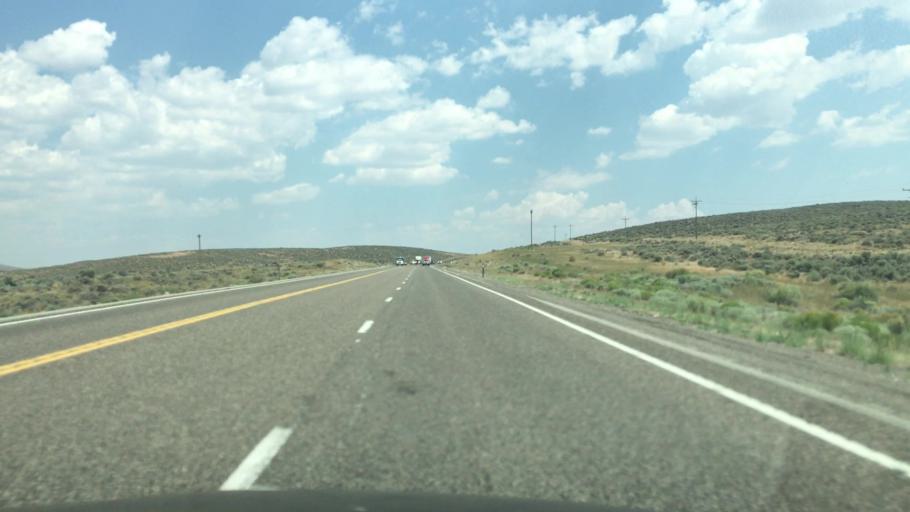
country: US
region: Nevada
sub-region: Elko County
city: Wells
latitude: 41.1820
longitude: -114.8758
